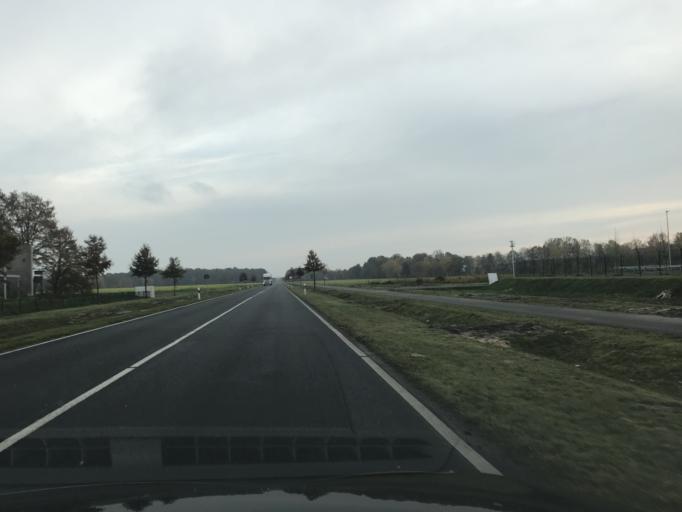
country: DE
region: North Rhine-Westphalia
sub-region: Regierungsbezirk Munster
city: Ladbergen
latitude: 52.1249
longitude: 7.6938
